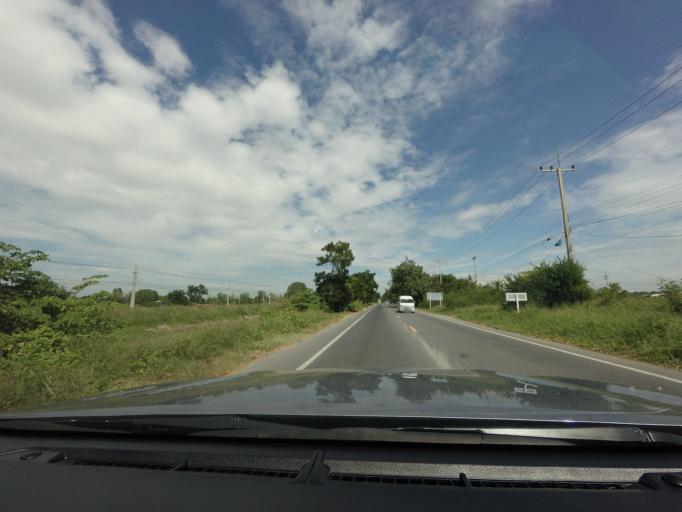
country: TH
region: Suphan Buri
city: Suphan Buri
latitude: 14.4558
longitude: 100.0852
